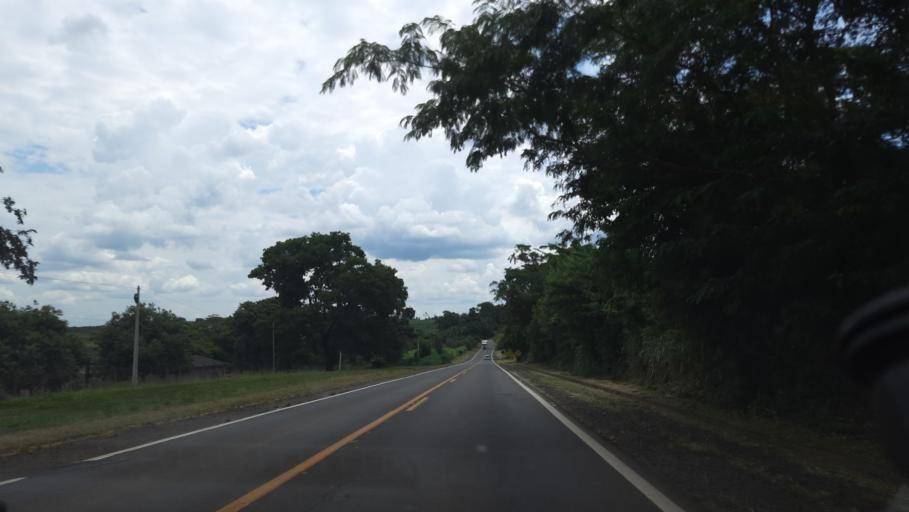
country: BR
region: Sao Paulo
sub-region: Mococa
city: Mococa
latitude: -21.4956
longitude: -47.0687
